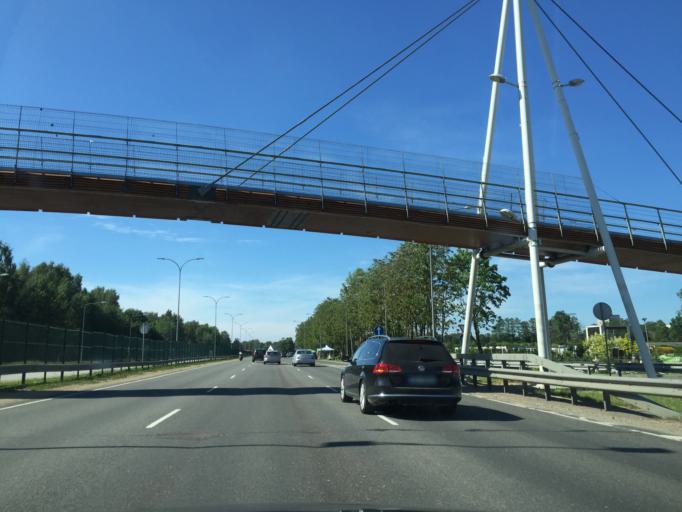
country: LV
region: Marupe
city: Marupe
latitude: 56.9403
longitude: 23.9994
